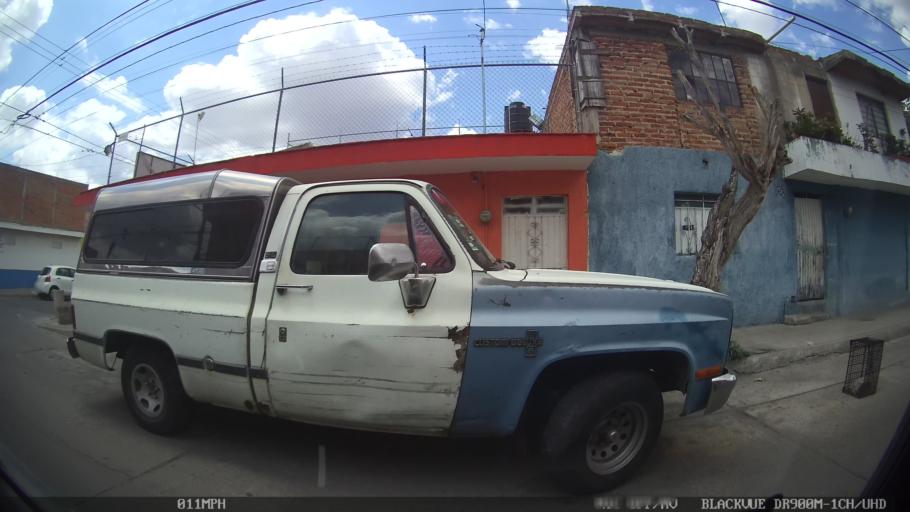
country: MX
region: Jalisco
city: Tlaquepaque
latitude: 20.6506
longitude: -103.2783
